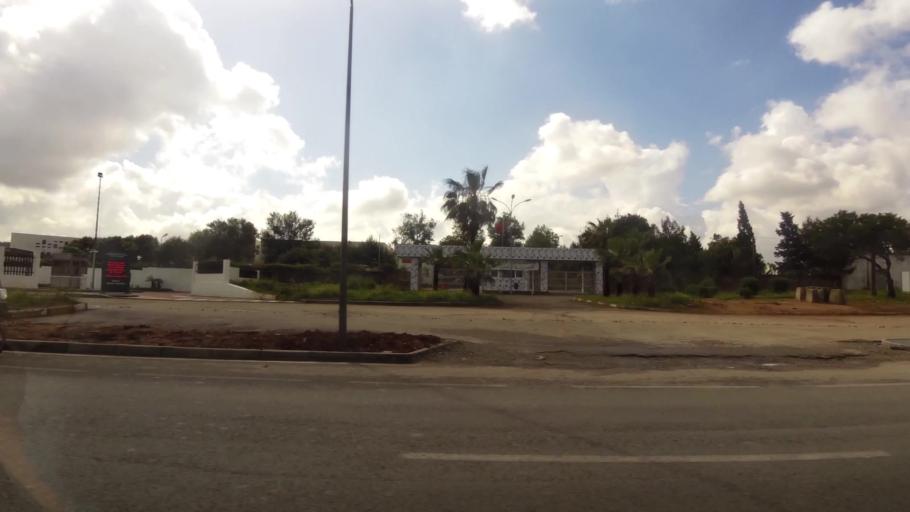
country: MA
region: Grand Casablanca
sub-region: Casablanca
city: Casablanca
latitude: 33.5398
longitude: -7.6597
